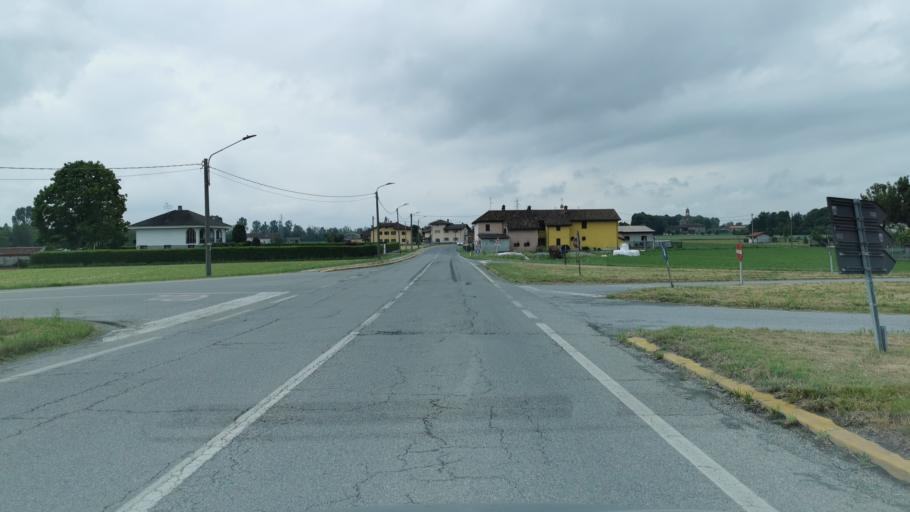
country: IT
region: Piedmont
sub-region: Provincia di Cuneo
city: Savigliano
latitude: 44.6349
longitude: 7.6423
